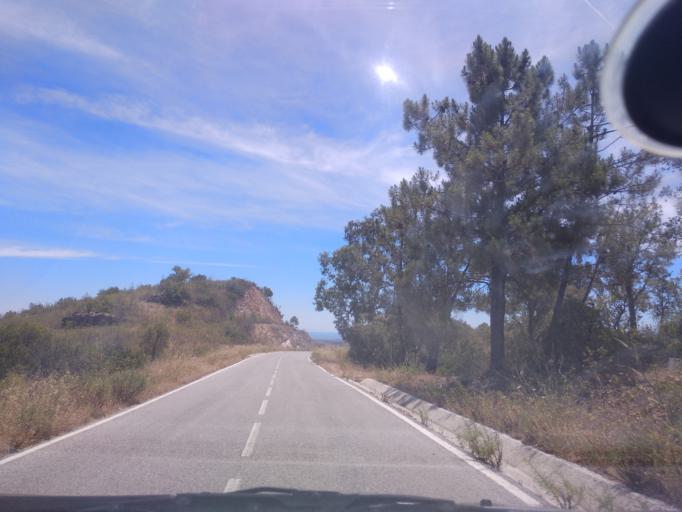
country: PT
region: Faro
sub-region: Sao Bras de Alportel
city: Sao Bras de Alportel
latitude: 37.1992
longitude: -7.8064
